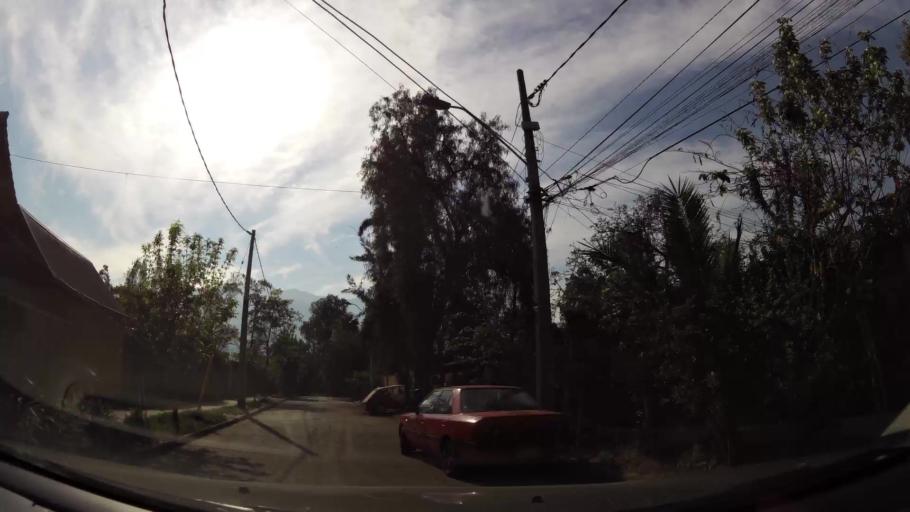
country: CL
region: Santiago Metropolitan
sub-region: Provincia de Cordillera
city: Puente Alto
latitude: -33.5607
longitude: -70.5604
